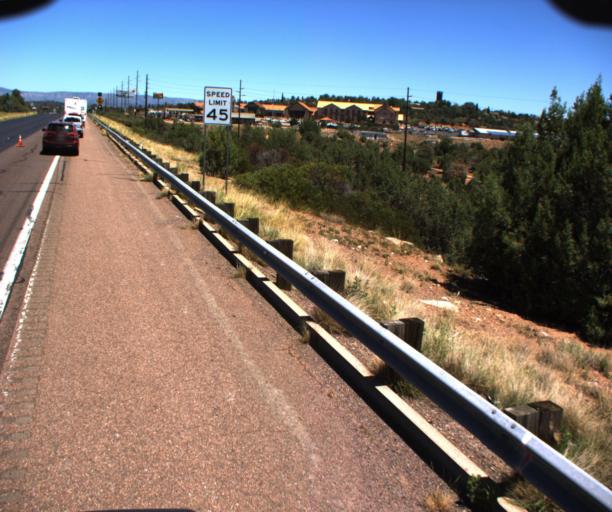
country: US
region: Arizona
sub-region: Gila County
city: Payson
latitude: 34.2162
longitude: -111.3318
